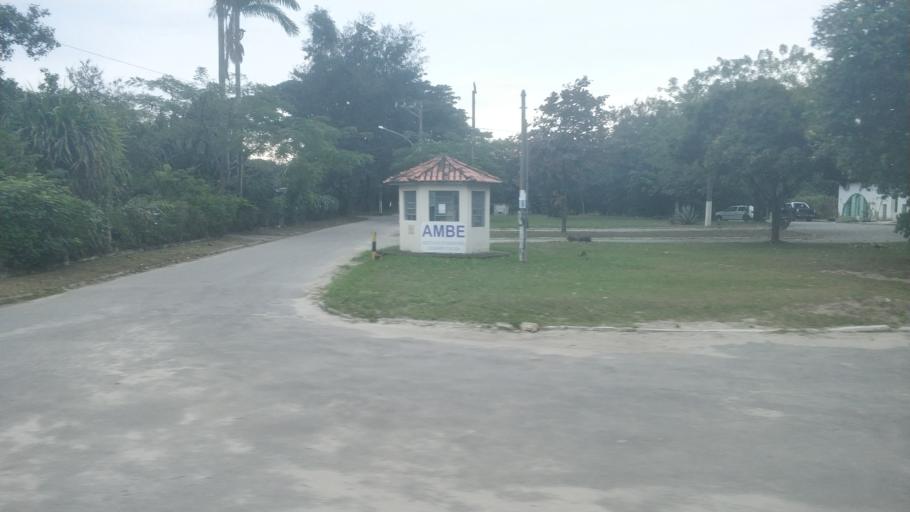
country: BR
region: Rio de Janeiro
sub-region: Seropedica
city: Seropedica
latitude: -22.7675
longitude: -43.6780
